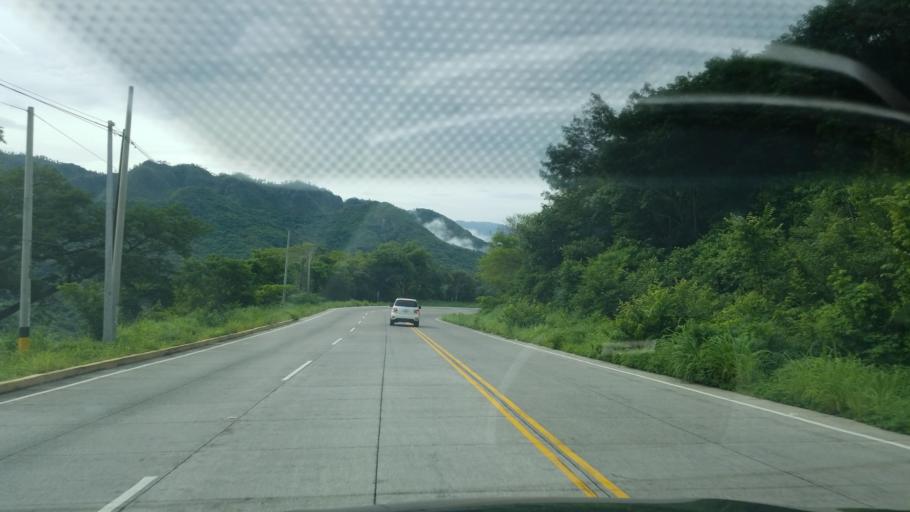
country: HN
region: Francisco Morazan
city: El Porvenir
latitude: 13.7165
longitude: -87.3178
